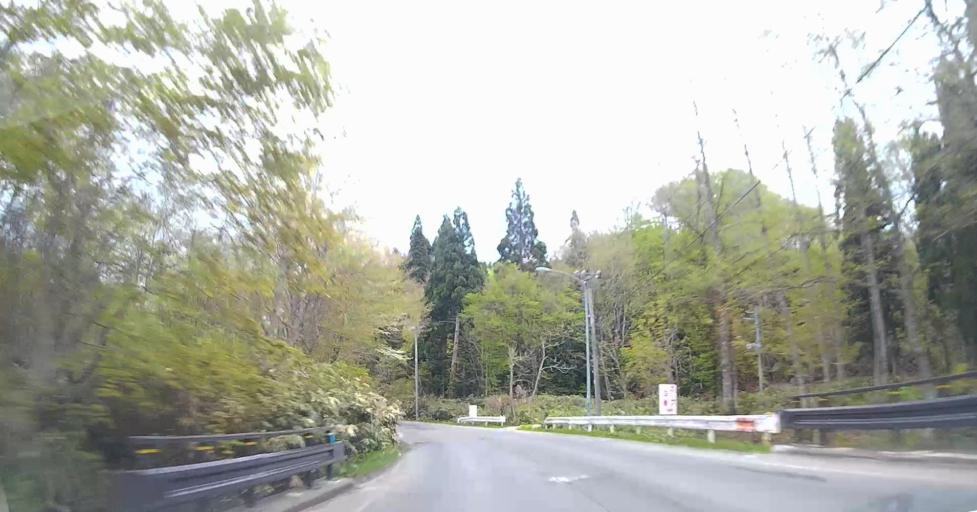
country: JP
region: Aomori
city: Goshogawara
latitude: 41.1138
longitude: 140.5295
